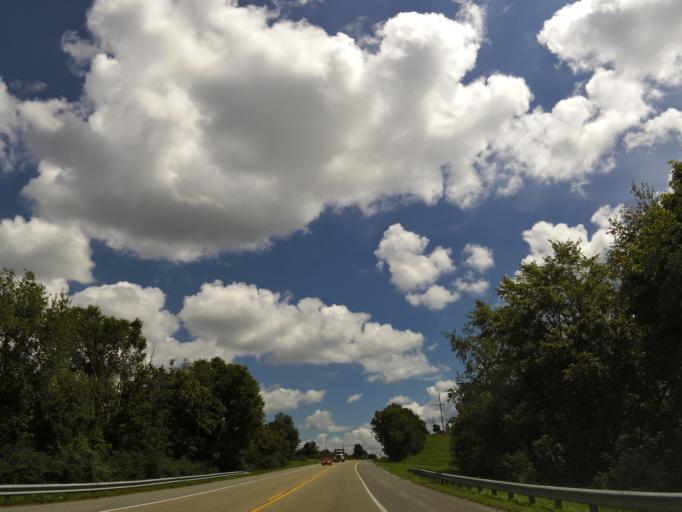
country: US
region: Kentucky
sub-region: Bell County
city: Middlesboro
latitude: 36.5274
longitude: -83.7396
